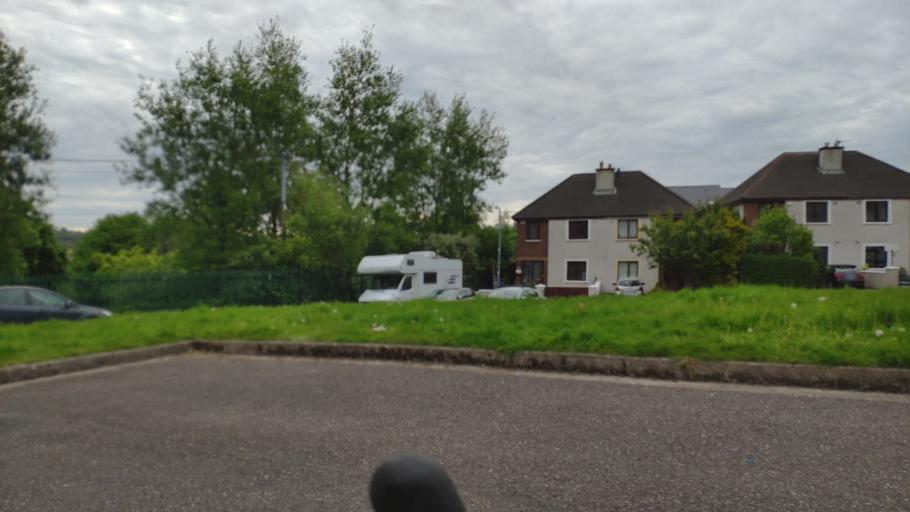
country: IE
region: Munster
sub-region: County Cork
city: Cork
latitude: 51.9111
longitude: -8.4566
